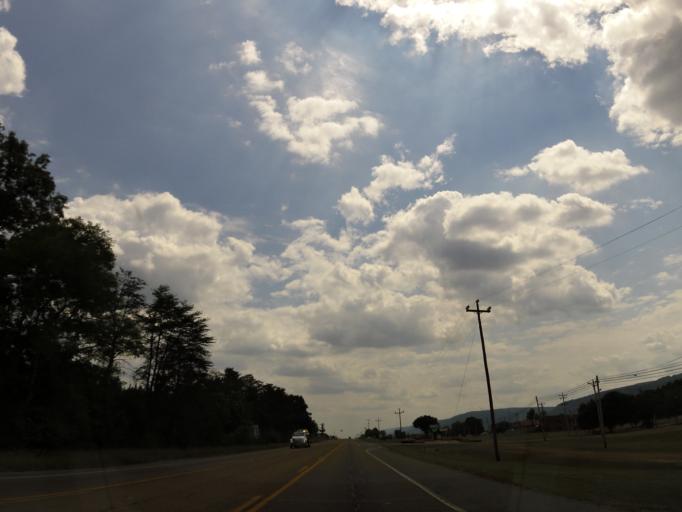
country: US
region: Tennessee
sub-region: Sequatchie County
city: Dunlap
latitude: 35.3570
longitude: -85.3989
